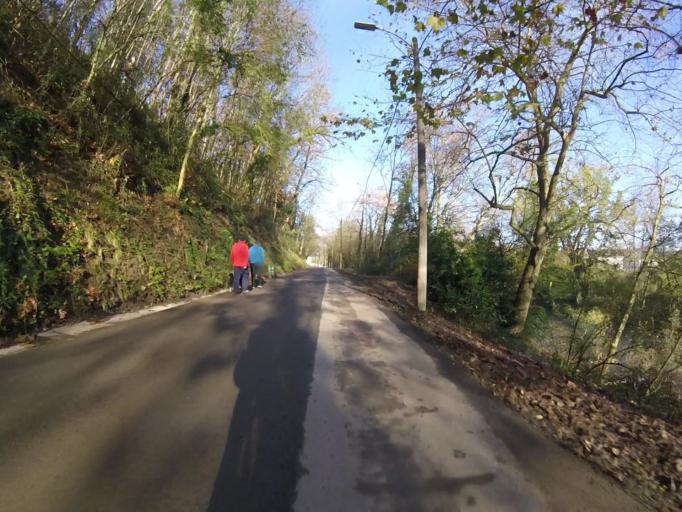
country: ES
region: Basque Country
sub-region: Provincia de Guipuzcoa
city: Usurbil
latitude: 43.2636
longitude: -2.0537
